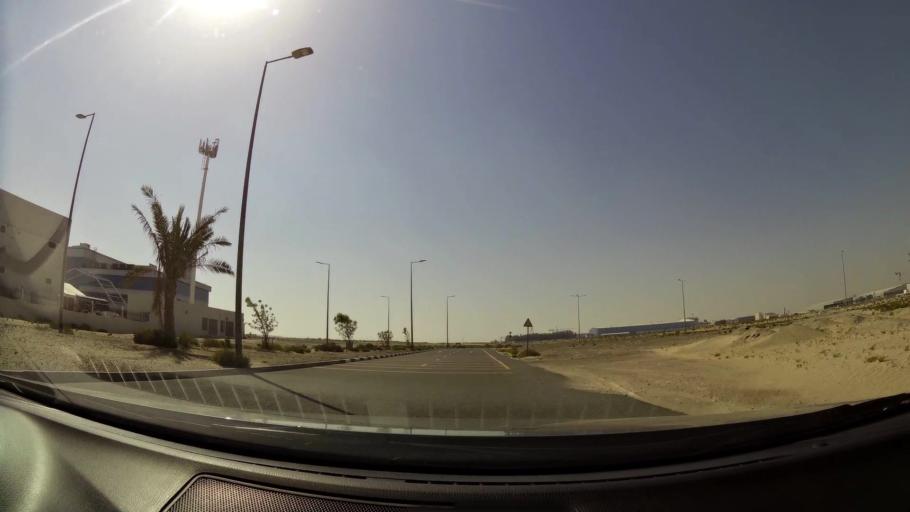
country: AE
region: Dubai
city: Dubai
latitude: 24.9267
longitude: 55.0593
